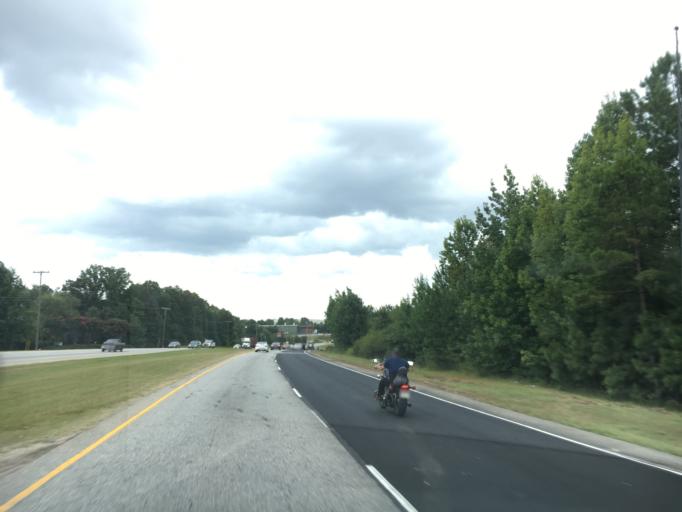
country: US
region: South Carolina
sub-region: Spartanburg County
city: Duncan
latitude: 34.9023
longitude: -82.1720
